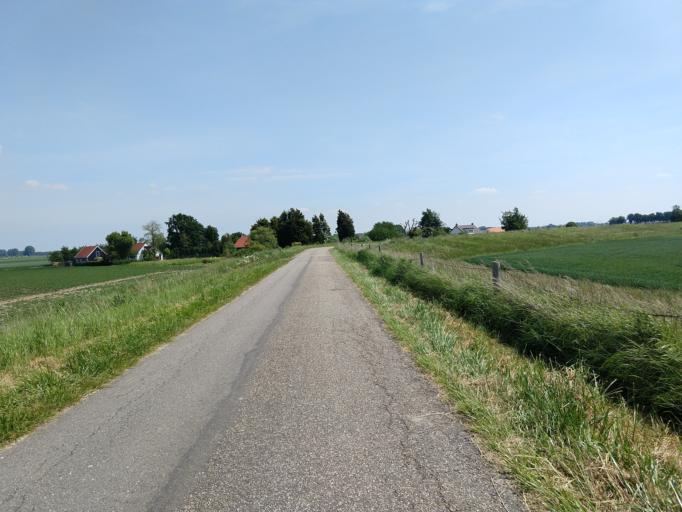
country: NL
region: Zeeland
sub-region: Gemeente Borsele
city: Borssele
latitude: 51.4724
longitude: 3.7596
